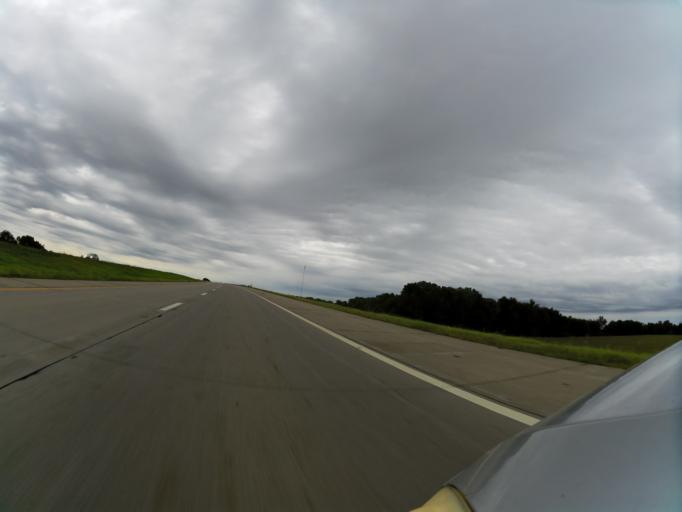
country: US
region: Kansas
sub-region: Reno County
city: Haven
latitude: 37.8743
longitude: -97.6942
